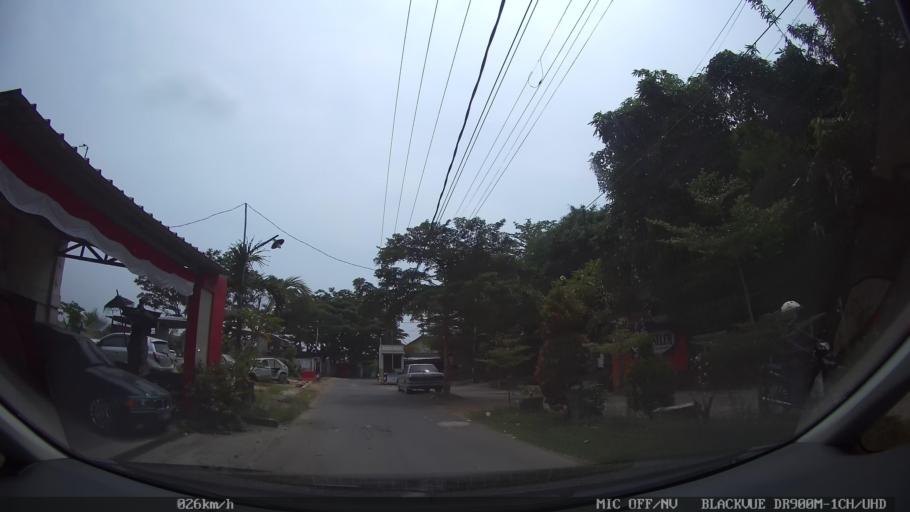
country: ID
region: Lampung
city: Kedaton
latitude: -5.4040
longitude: 105.3210
